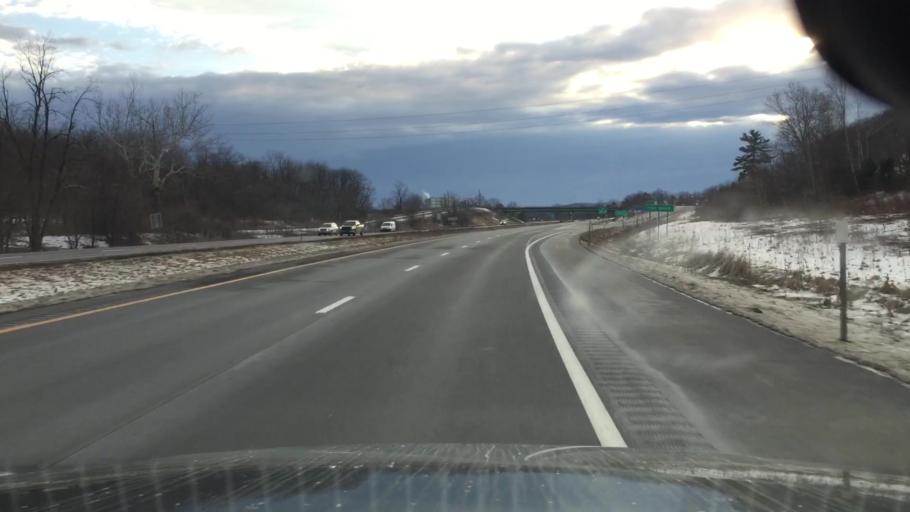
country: US
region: Pennsylvania
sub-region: Bradford County
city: South Waverly
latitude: 42.0003
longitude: -76.5545
